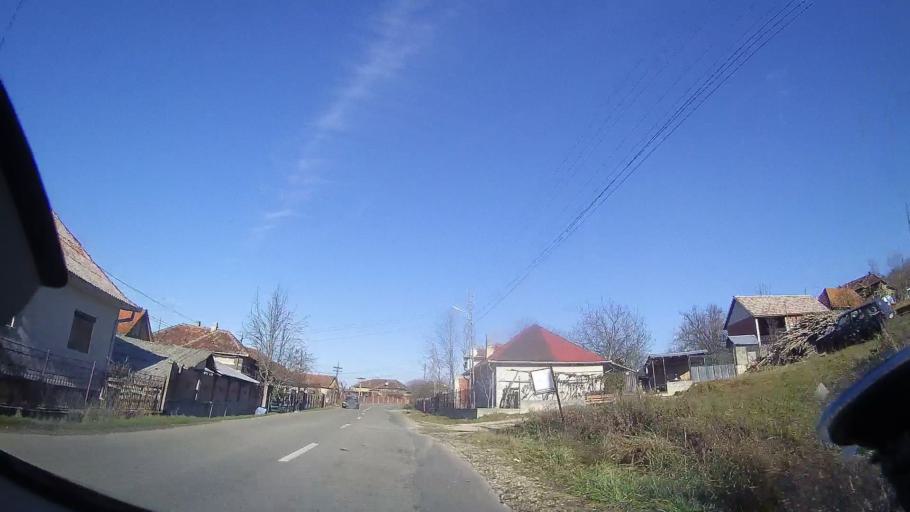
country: RO
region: Bihor
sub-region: Comuna Bratca
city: Bratca
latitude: 46.9341
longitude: 22.6032
